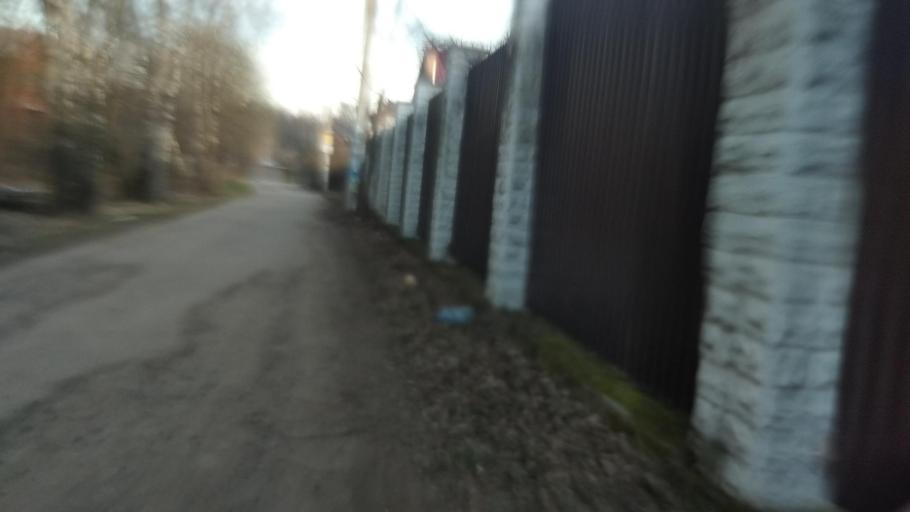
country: RU
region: Moskovskaya
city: Razvilka
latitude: 55.5725
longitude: 37.7435
